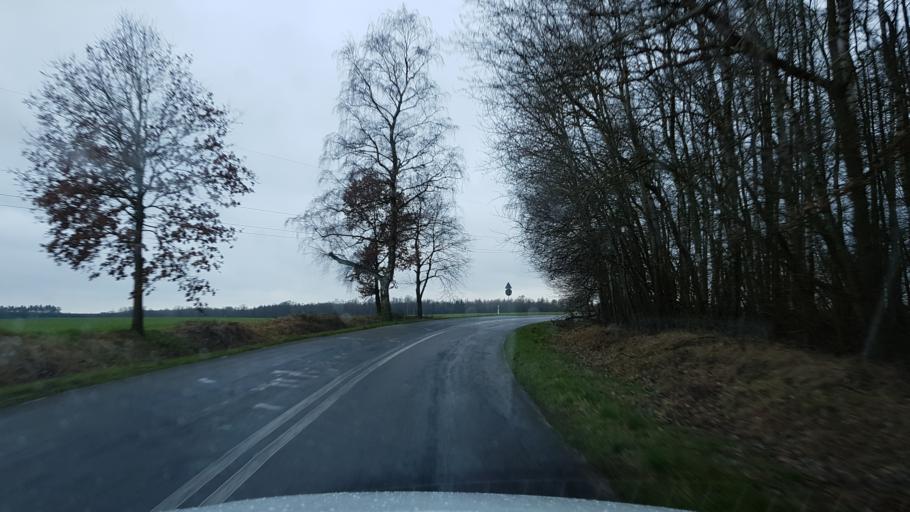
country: PL
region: West Pomeranian Voivodeship
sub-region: Powiat lobeski
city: Radowo Male
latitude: 53.6048
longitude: 15.4486
